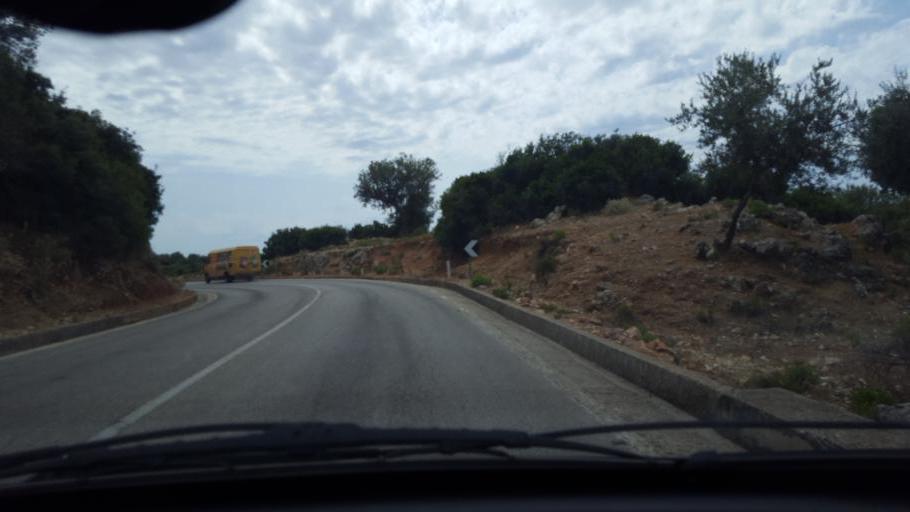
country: AL
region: Vlore
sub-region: Rrethi i Sarandes
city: Lukove
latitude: 40.0289
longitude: 19.8865
